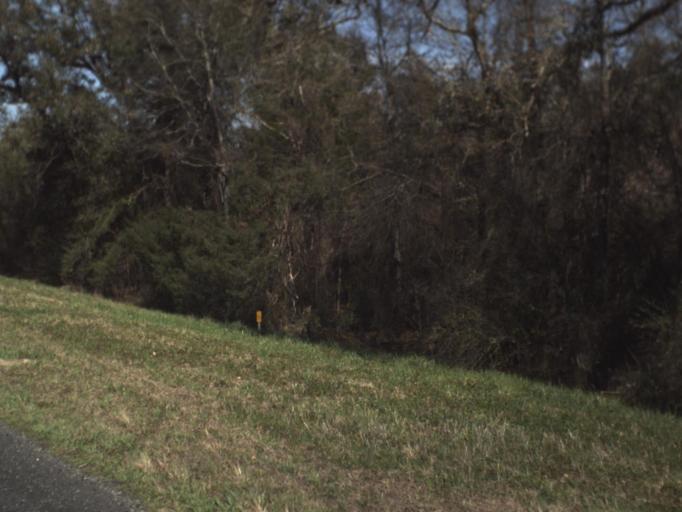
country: US
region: Florida
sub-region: Jackson County
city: Graceville
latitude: 30.9403
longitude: -85.3915
